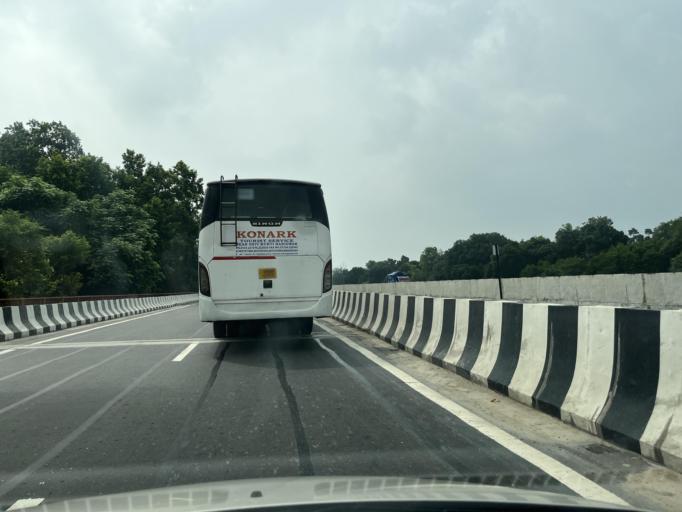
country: IN
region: Uttarakhand
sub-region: Dehradun
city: Raiwala
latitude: 30.0682
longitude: 78.2076
